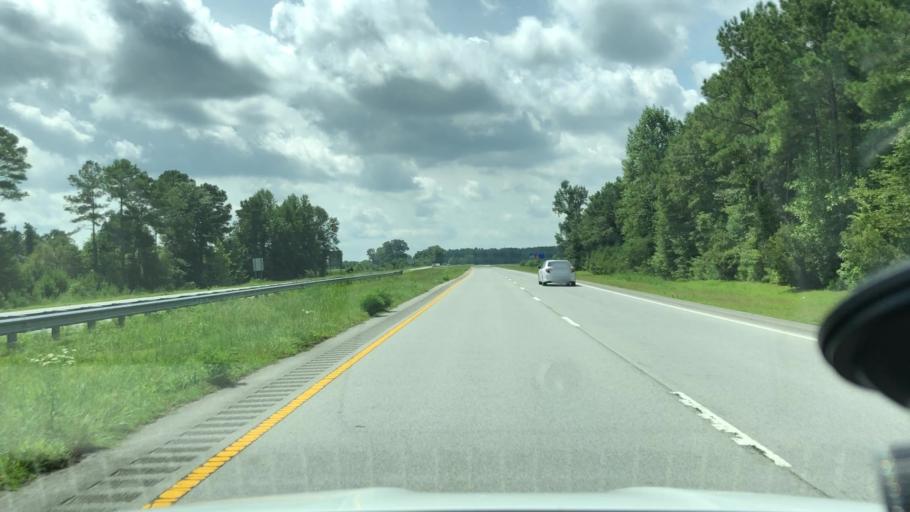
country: US
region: North Carolina
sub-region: Beaufort County
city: Washington
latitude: 35.5156
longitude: -77.0862
